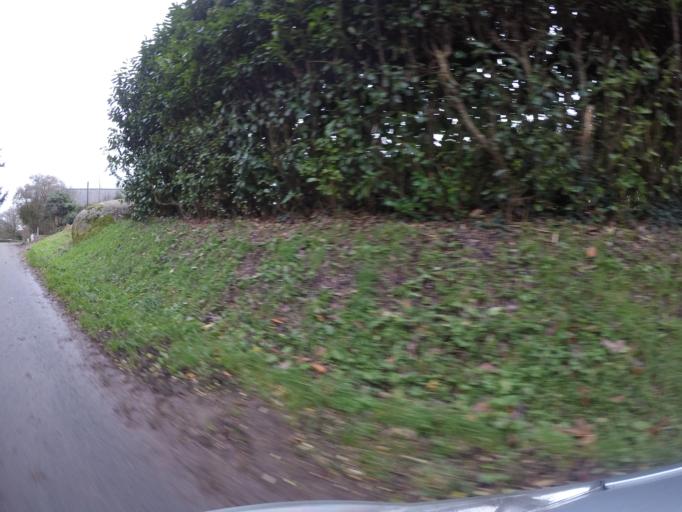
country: FR
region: Brittany
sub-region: Departement des Cotes-d'Armor
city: Callac
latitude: 48.4033
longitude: -3.3540
